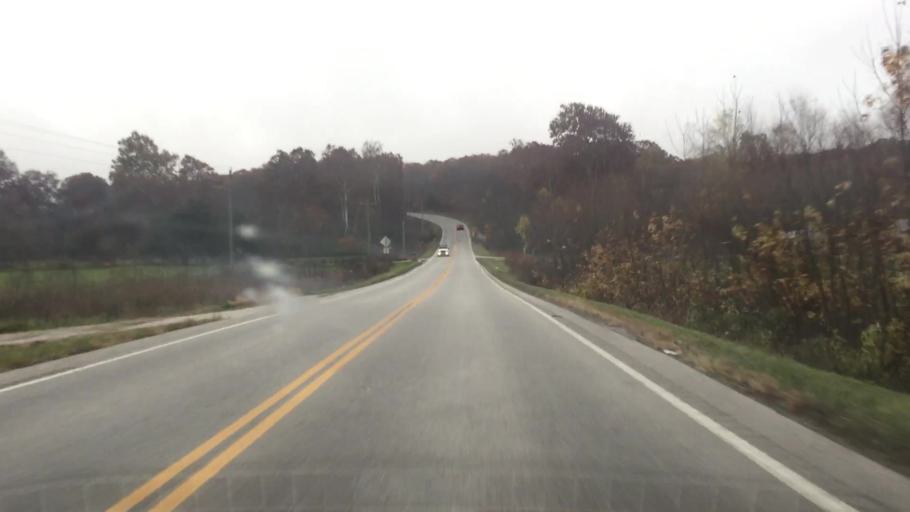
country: US
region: Missouri
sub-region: Callaway County
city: Fulton
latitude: 38.8818
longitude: -92.0907
